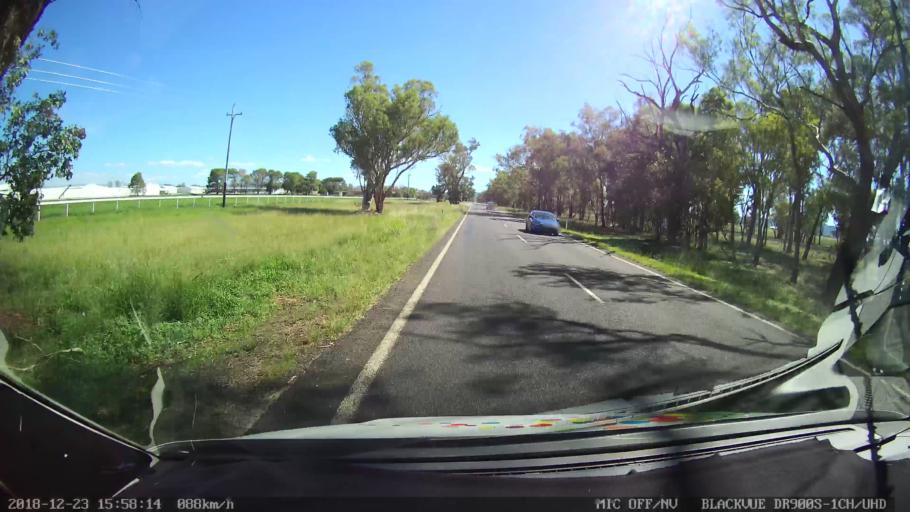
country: AU
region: New South Wales
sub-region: Tamworth Municipality
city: Phillip
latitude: -31.1861
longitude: 150.8433
